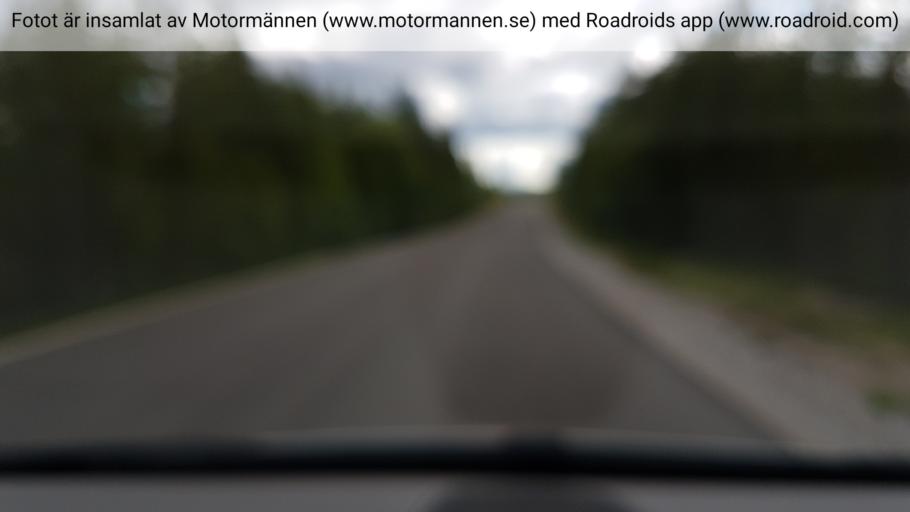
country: SE
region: Jaemtland
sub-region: Harjedalens Kommun
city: Sveg
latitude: 61.6928
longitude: 14.1887
